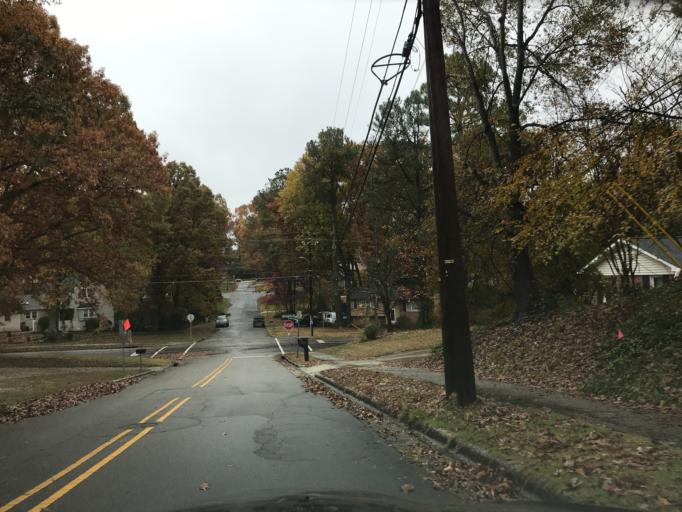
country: US
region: North Carolina
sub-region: Wake County
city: West Raleigh
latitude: 35.8373
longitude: -78.6219
